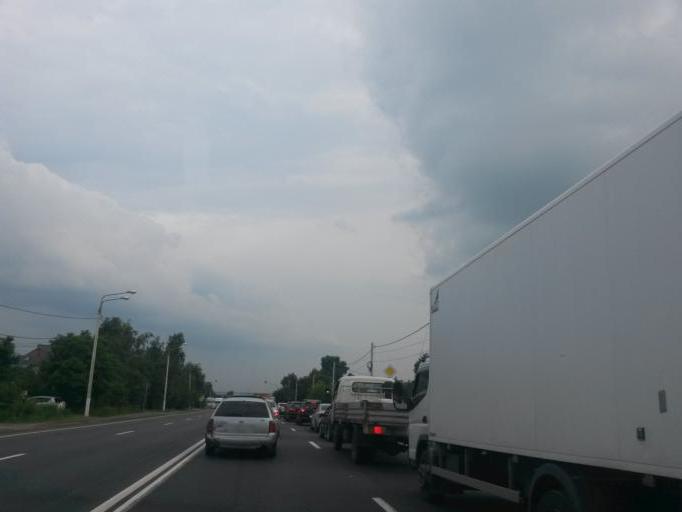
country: RU
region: Moskovskaya
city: Gorki-Leninskiye
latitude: 55.5098
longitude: 37.7553
